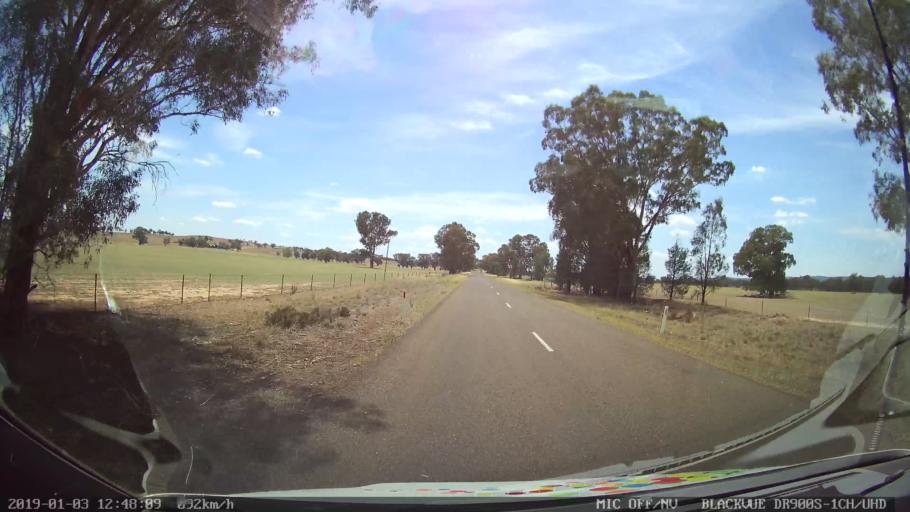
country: AU
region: New South Wales
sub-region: Weddin
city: Grenfell
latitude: -33.7180
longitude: 148.2480
